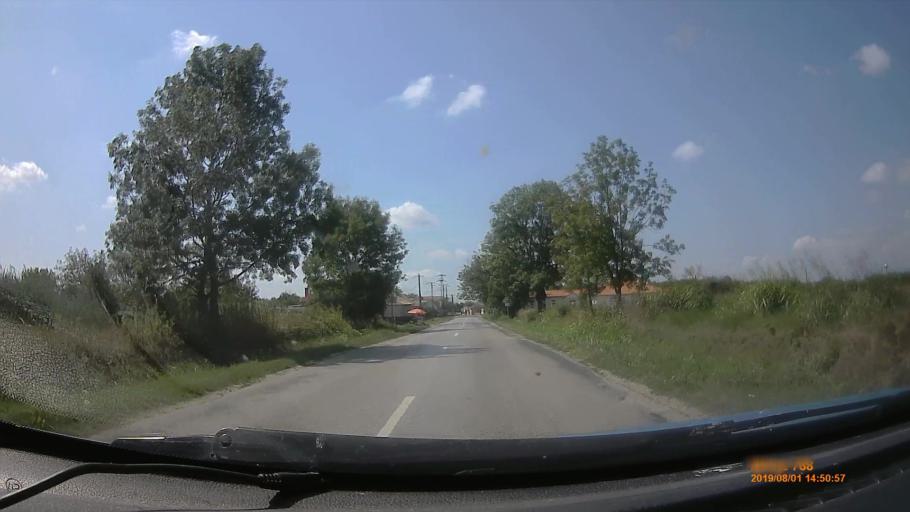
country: HU
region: Baranya
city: Vajszlo
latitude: 45.8538
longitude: 17.9990
